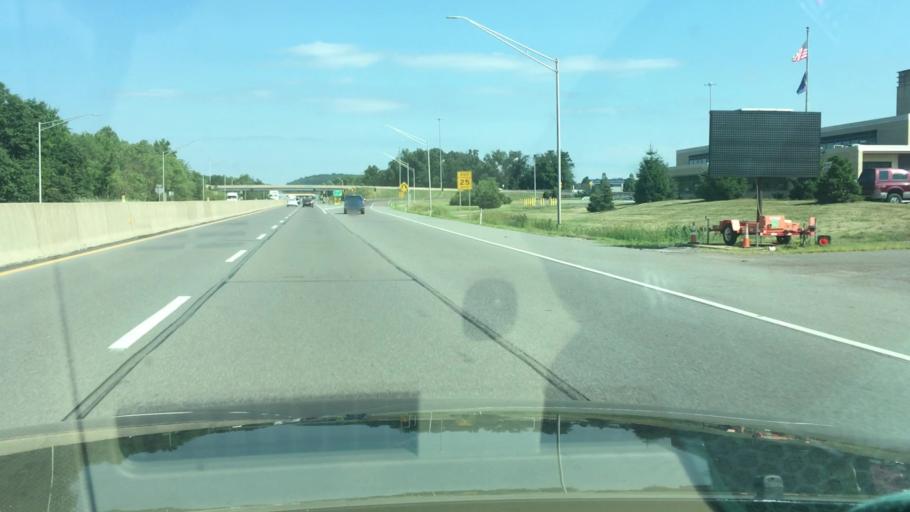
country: US
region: Pennsylvania
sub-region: Bucks County
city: Spinnerstown
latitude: 40.4352
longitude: -75.4240
